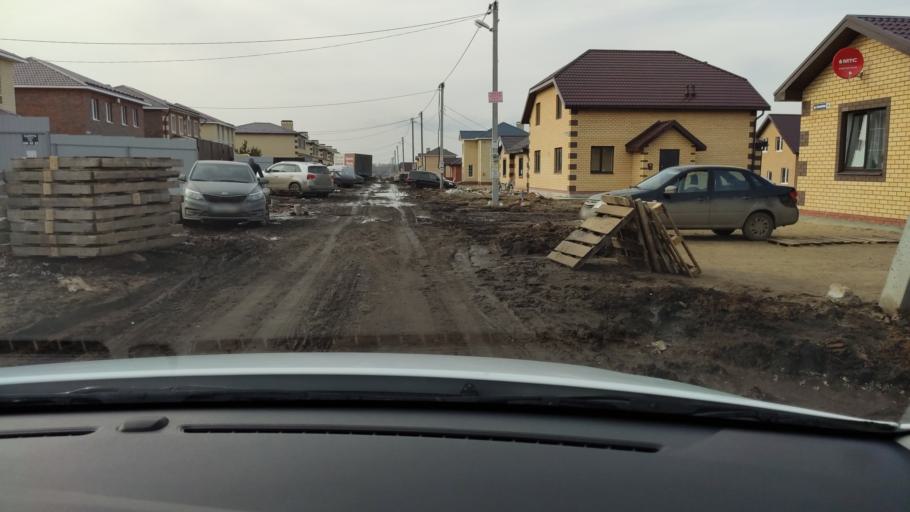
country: RU
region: Tatarstan
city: Stolbishchi
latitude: 55.7181
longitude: 49.3316
